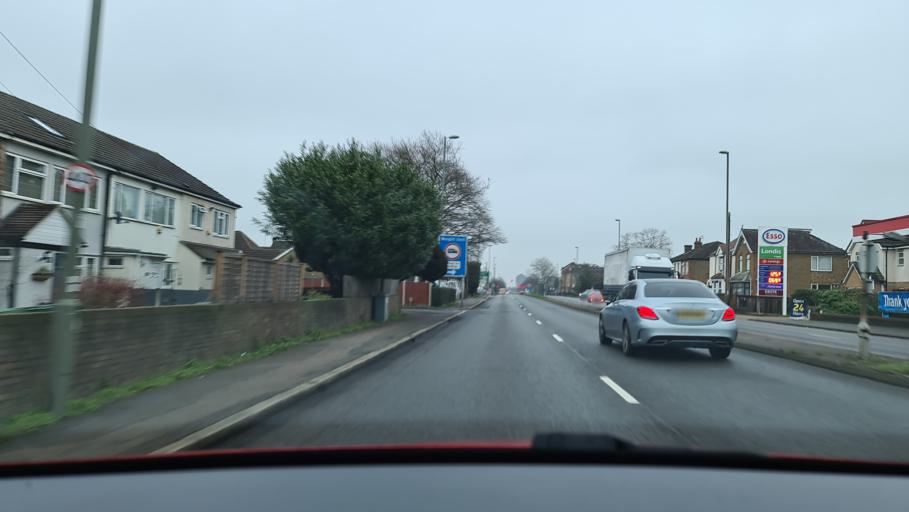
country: GB
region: England
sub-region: Surrey
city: Shepperton
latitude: 51.4226
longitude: -0.4452
